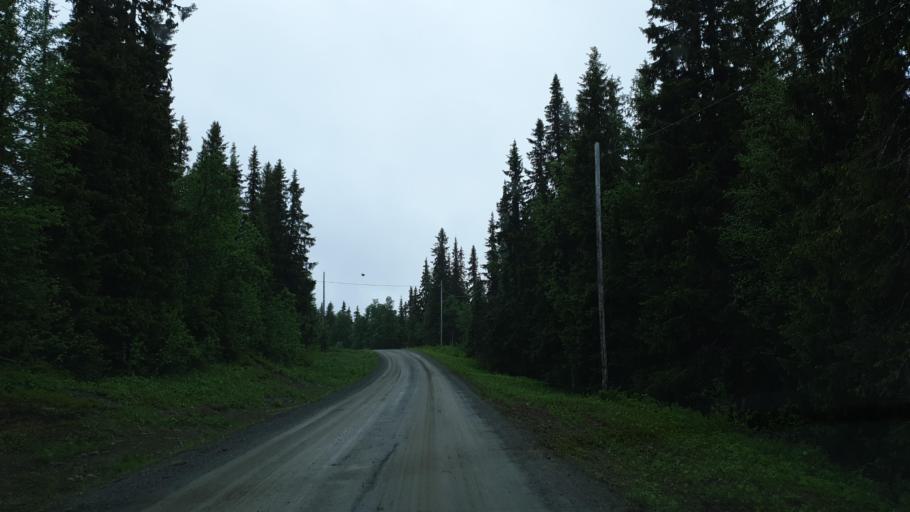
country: SE
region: Vaesterbotten
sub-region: Vilhelmina Kommun
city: Sjoberg
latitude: 65.3380
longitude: 15.8918
